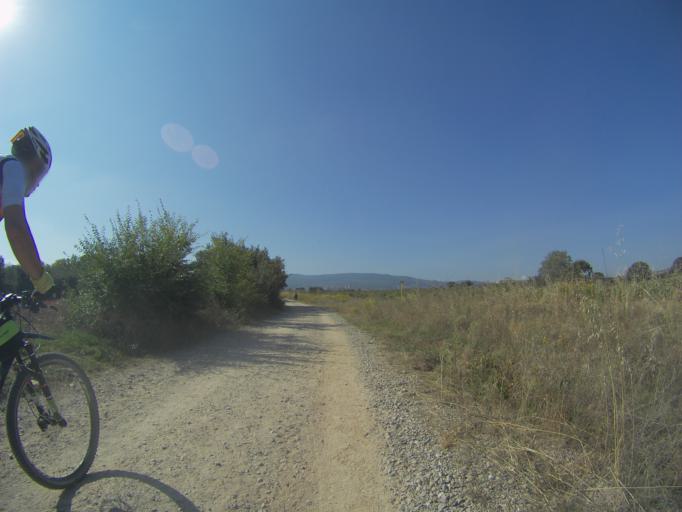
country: ES
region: La Rioja
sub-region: Provincia de La Rioja
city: Hornos de Moncalvillo
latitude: 42.4164
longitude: -2.5869
